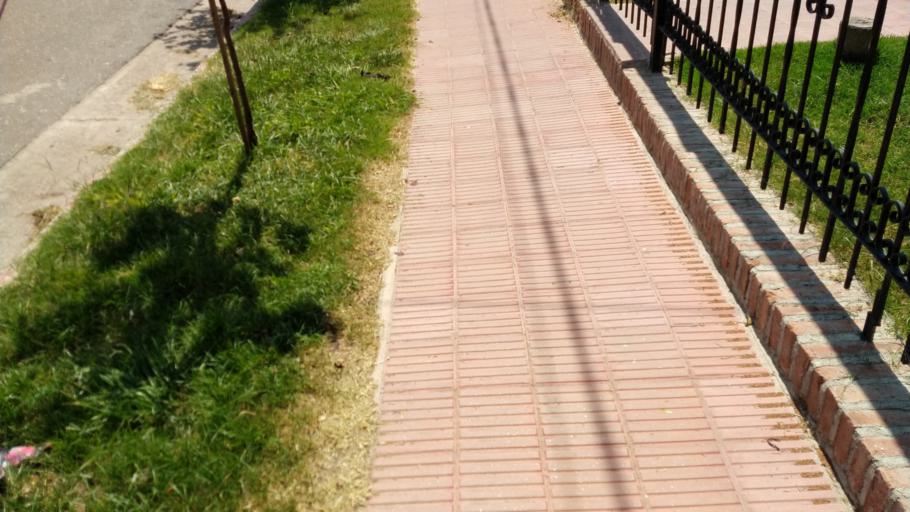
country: AR
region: Cordoba
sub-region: Departamento de Capital
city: Cordoba
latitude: -31.3617
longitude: -64.2288
